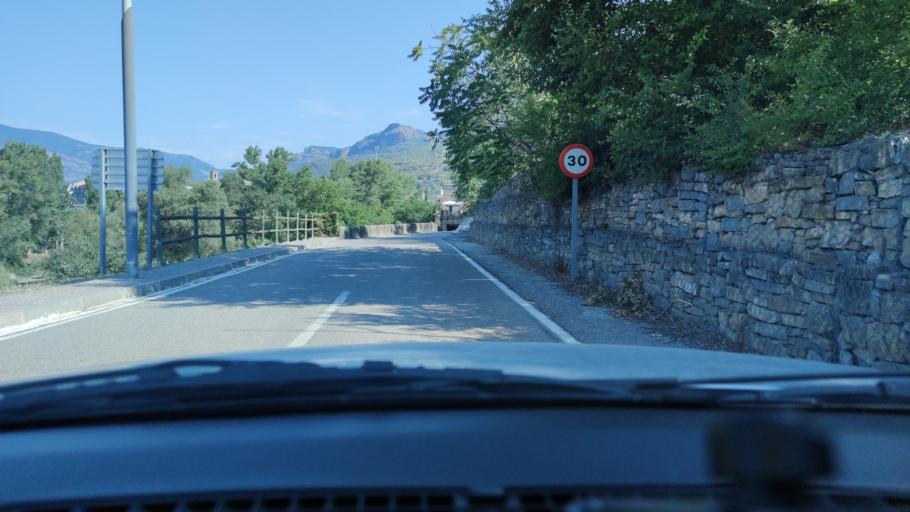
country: ES
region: Catalonia
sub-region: Provincia de Lleida
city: Senterada
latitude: 42.2427
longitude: 0.9716
